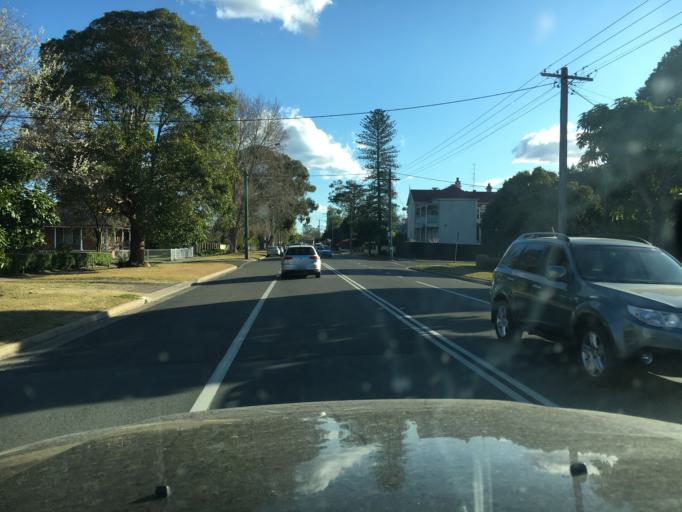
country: AU
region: New South Wales
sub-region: Maitland Municipality
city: Maitland
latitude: -32.7263
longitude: 151.5609
